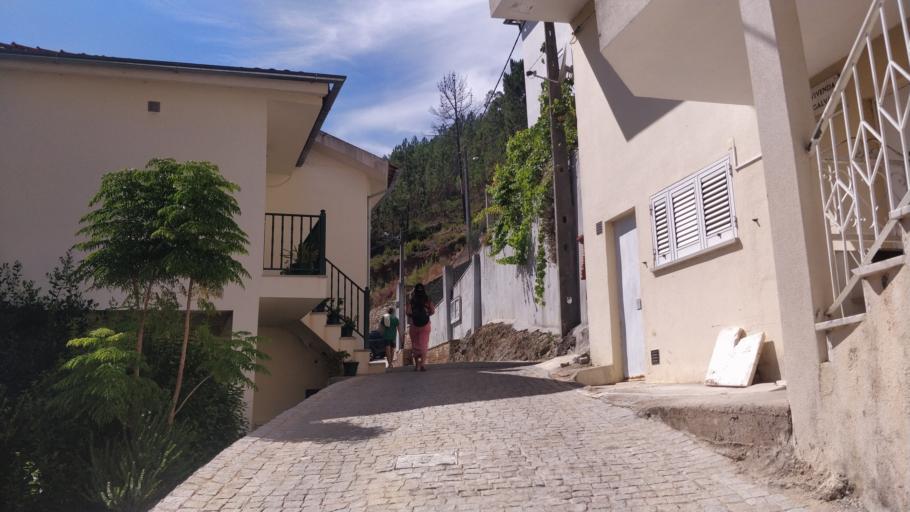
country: PT
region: Guarda
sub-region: Seia
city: Seia
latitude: 40.2859
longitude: -7.7219
